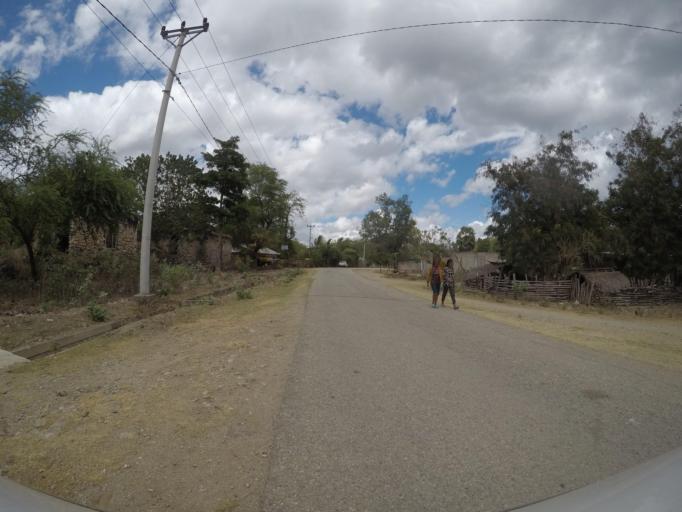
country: TL
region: Lautem
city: Lospalos
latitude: -8.3622
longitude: 126.9050
